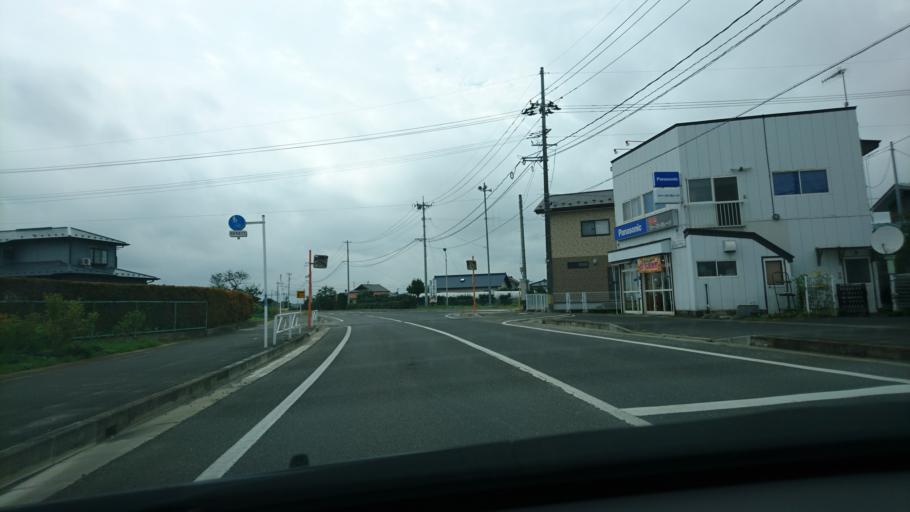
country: JP
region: Iwate
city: Ichinoseki
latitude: 38.7678
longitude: 141.1398
